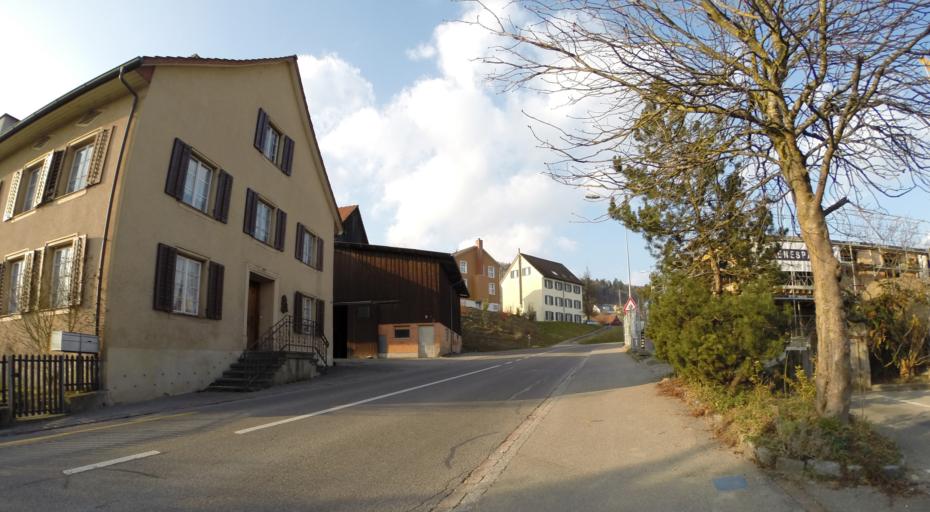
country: CH
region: Thurgau
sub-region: Frauenfeld District
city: Huttwilen
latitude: 47.6055
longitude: 8.9101
